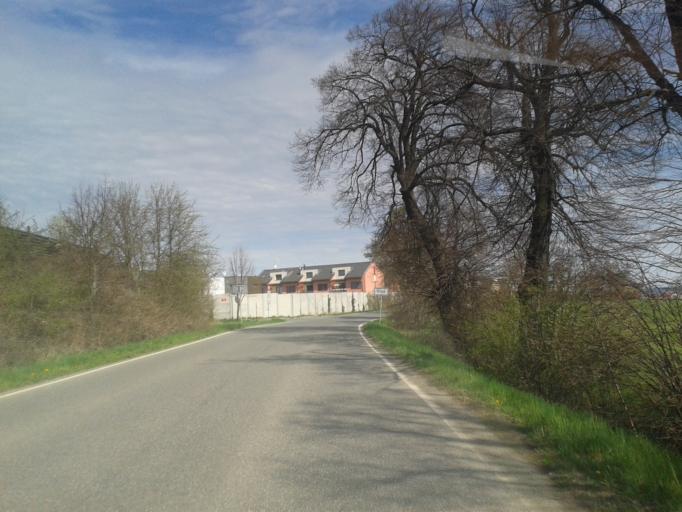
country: CZ
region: Central Bohemia
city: Mnisek pod Brdy
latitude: 49.8874
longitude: 14.2823
